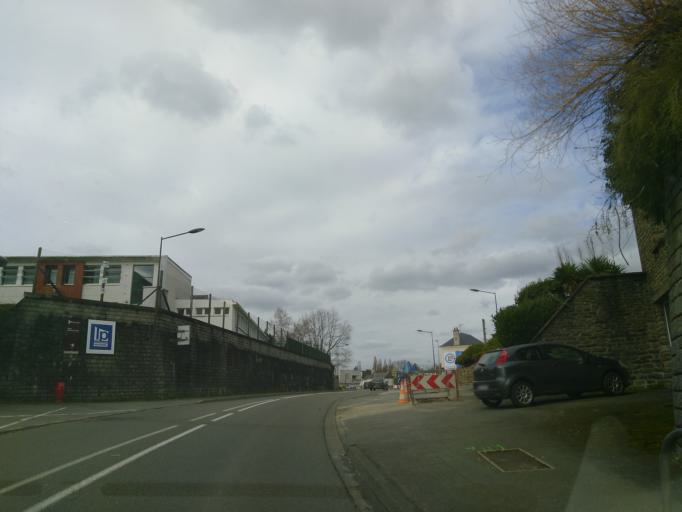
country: FR
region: Pays de la Loire
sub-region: Departement de la Mayenne
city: Mayenne
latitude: 48.3004
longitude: -0.6224
